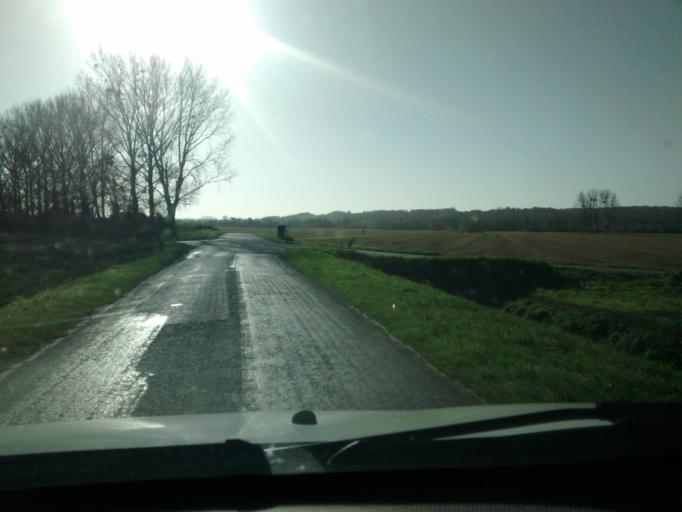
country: FR
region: Brittany
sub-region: Departement d'Ille-et-Vilaine
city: Roz-sur-Couesnon
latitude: 48.5975
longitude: -1.5636
